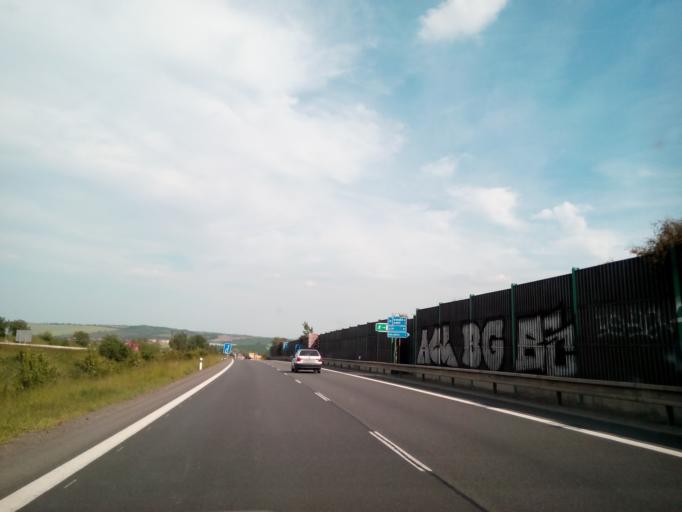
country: CZ
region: South Moravian
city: Blazovice
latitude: 49.1802
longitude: 16.8122
